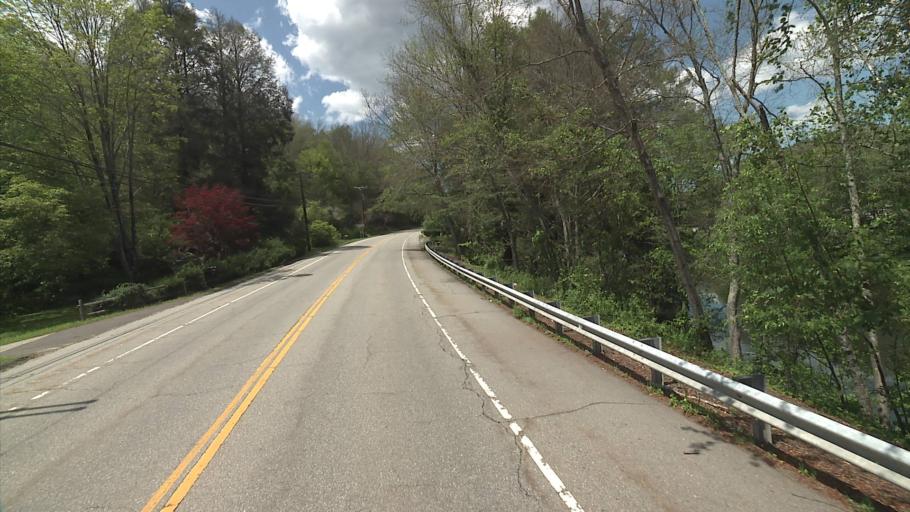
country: US
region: Connecticut
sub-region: Middlesex County
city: Moodus
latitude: 41.5142
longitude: -72.4832
